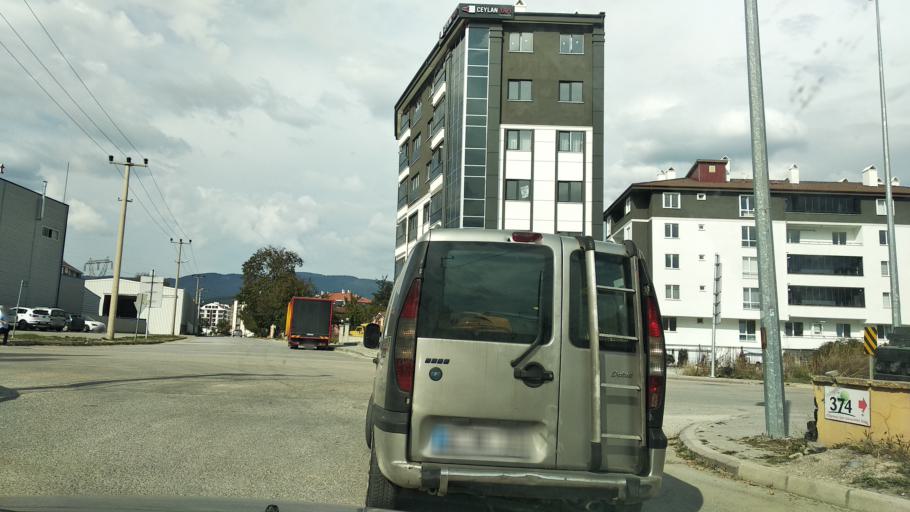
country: TR
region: Bolu
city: Bolu
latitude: 40.7302
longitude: 31.5855
